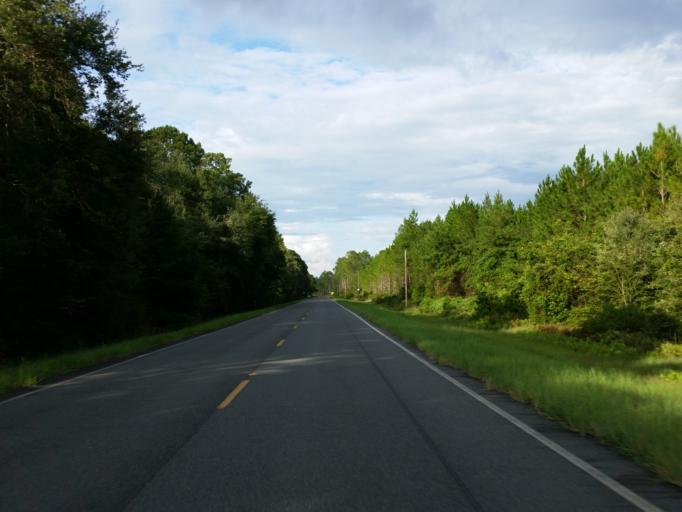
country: US
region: Florida
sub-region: Hamilton County
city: Jasper
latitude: 30.6360
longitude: -82.5871
